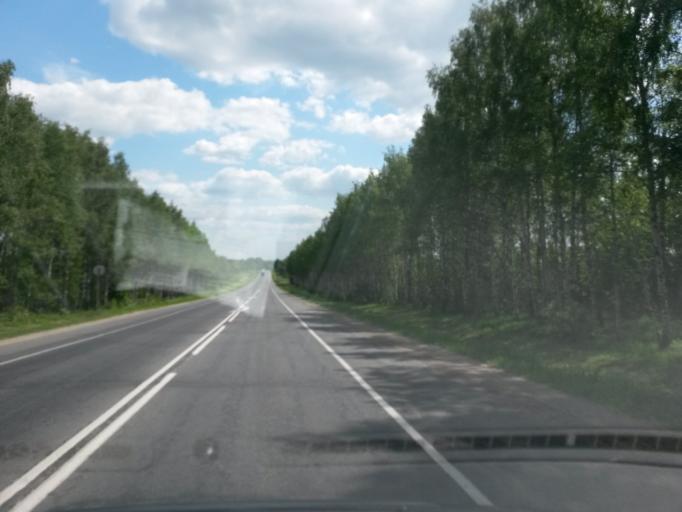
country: RU
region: Jaroslavl
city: Yaroslavl
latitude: 57.5580
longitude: 39.8613
